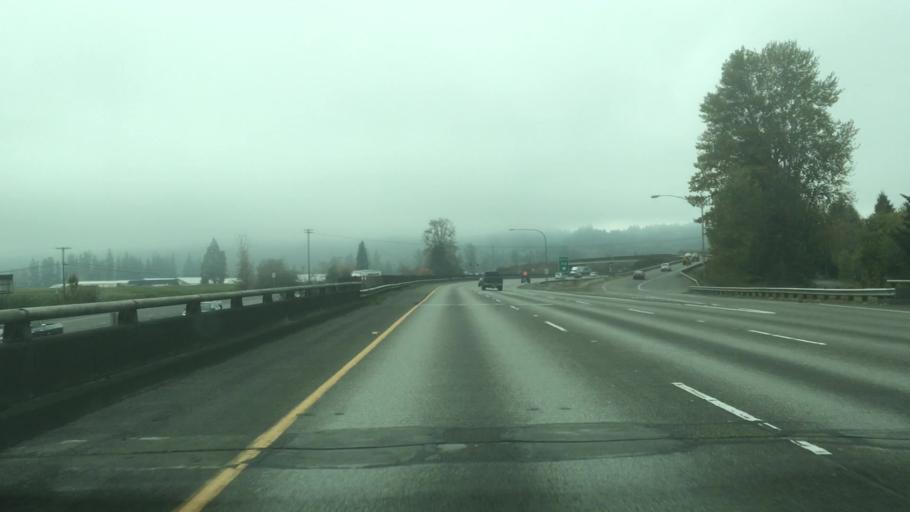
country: US
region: Washington
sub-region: Thurston County
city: Tanglewilde-Thompson Place
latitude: 47.0692
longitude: -122.7110
